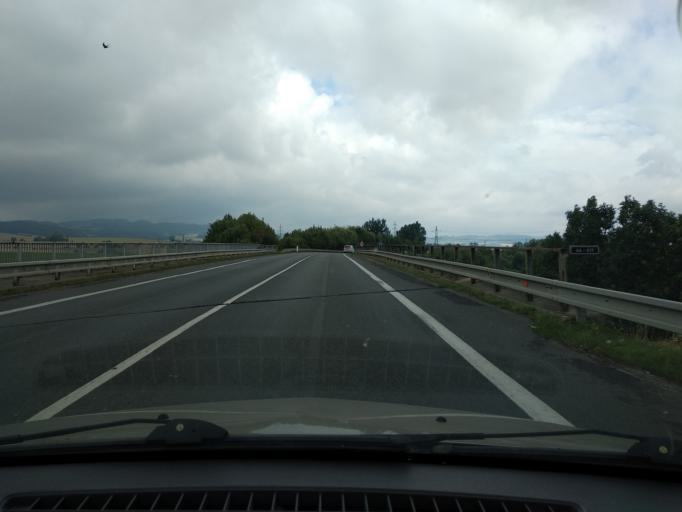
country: CZ
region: Olomoucky
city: Zabreh
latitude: 49.8871
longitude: 16.8924
